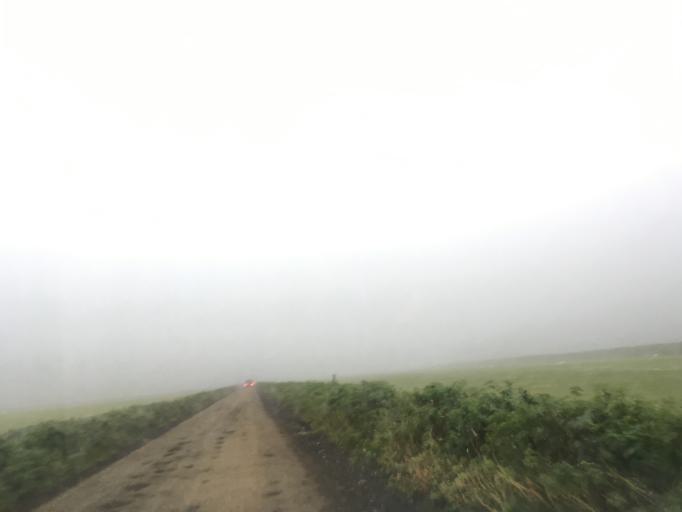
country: IS
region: South
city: Vestmannaeyjar
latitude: 63.4423
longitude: -18.9042
